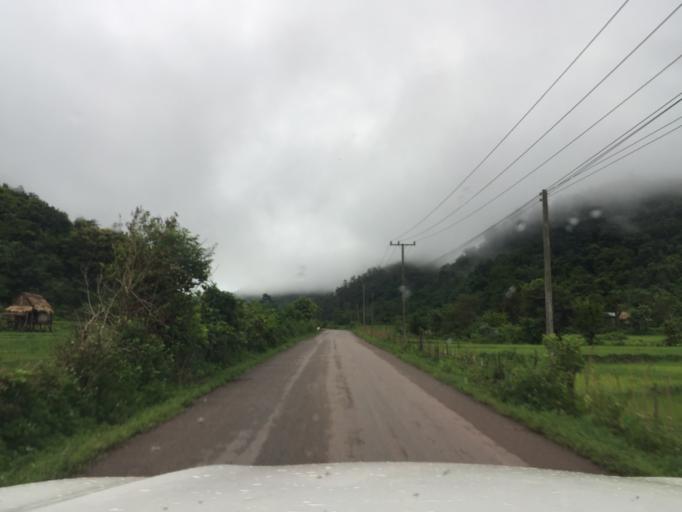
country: LA
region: Oudomxai
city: Muang La
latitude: 20.8273
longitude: 102.0975
